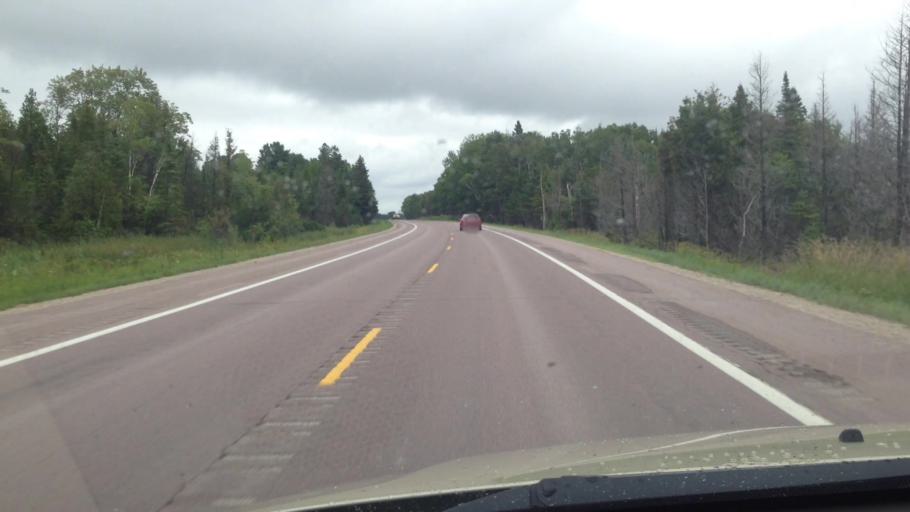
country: US
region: Michigan
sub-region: Schoolcraft County
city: Manistique
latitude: 45.9873
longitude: -86.1047
